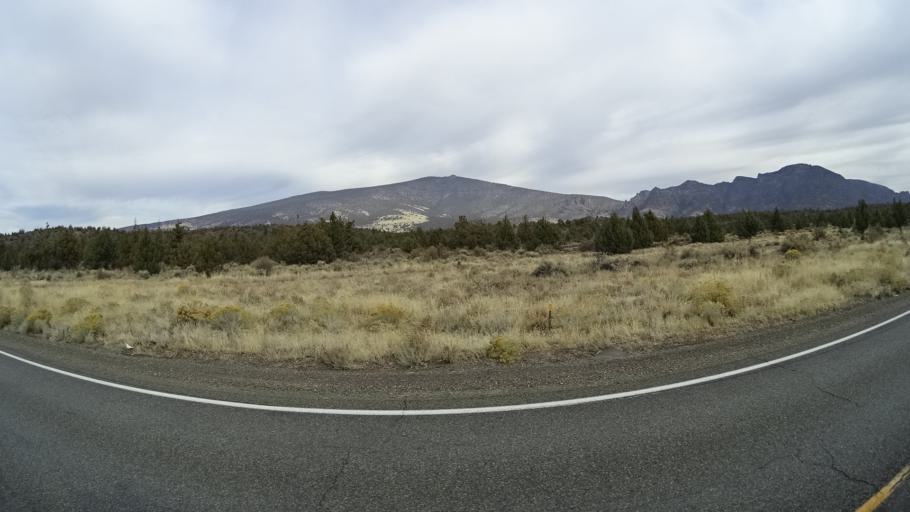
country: US
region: California
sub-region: Siskiyou County
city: Weed
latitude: 41.5732
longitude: -122.2771
